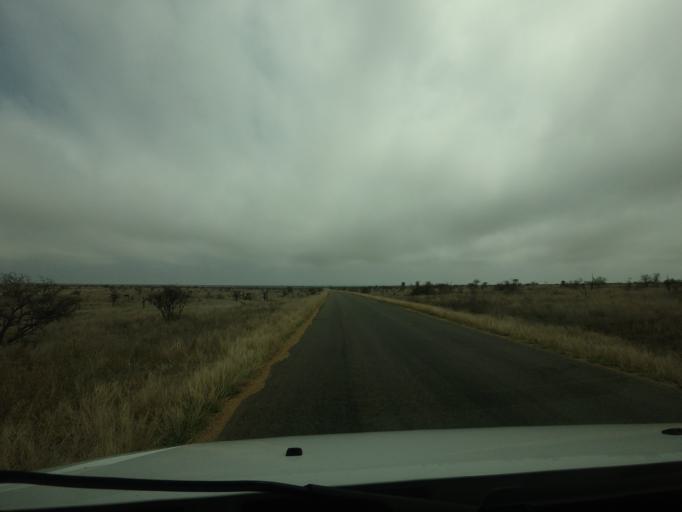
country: ZA
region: Limpopo
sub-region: Mopani District Municipality
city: Phalaborwa
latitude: -24.2117
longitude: 31.7200
